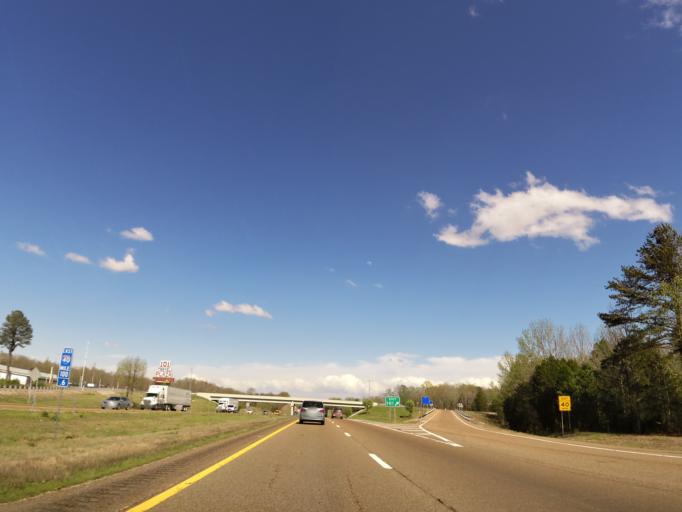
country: US
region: Tennessee
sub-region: Henderson County
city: Lexington
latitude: 35.7540
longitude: -88.5163
